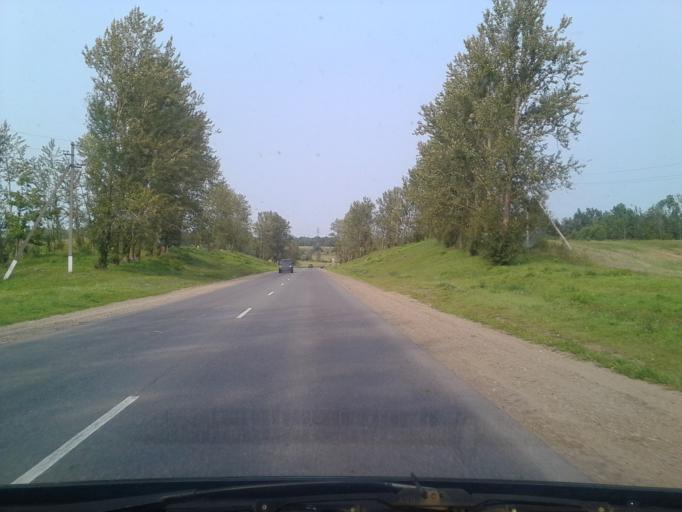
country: BY
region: Minsk
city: Hatava
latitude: 53.7967
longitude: 27.6471
